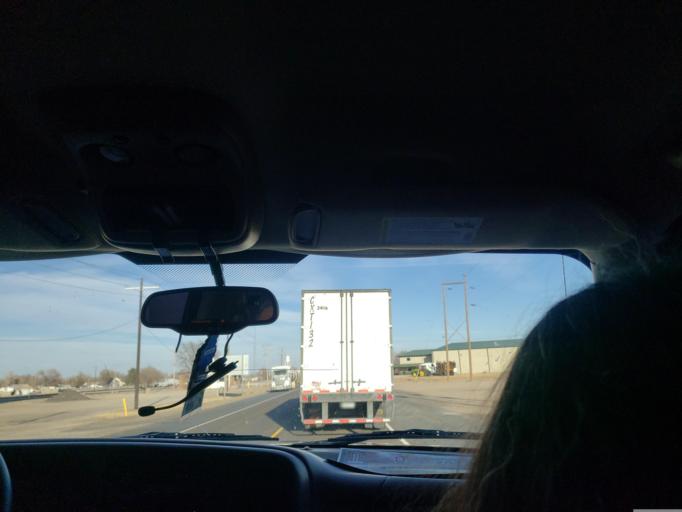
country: US
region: Oklahoma
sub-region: Texas County
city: Goodwell
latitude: 36.5001
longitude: -101.7892
